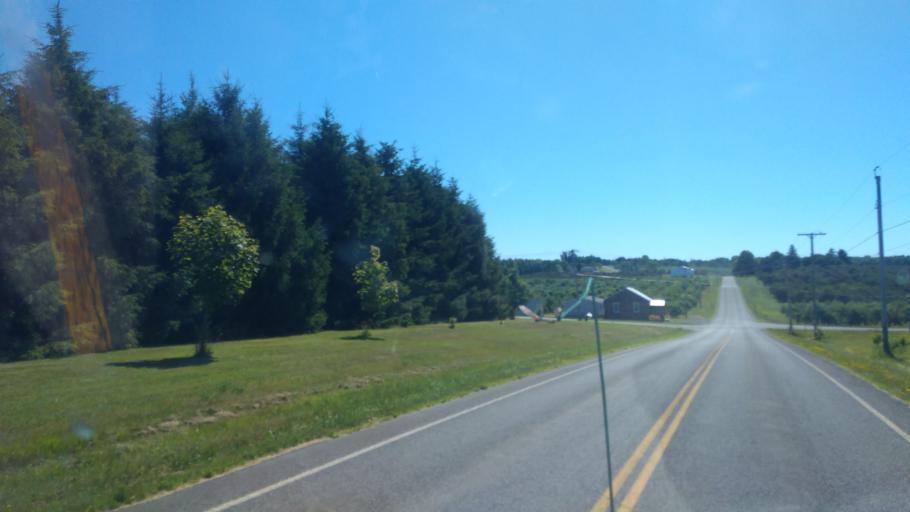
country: US
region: New York
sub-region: Wayne County
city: Sodus
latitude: 43.2758
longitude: -77.1148
